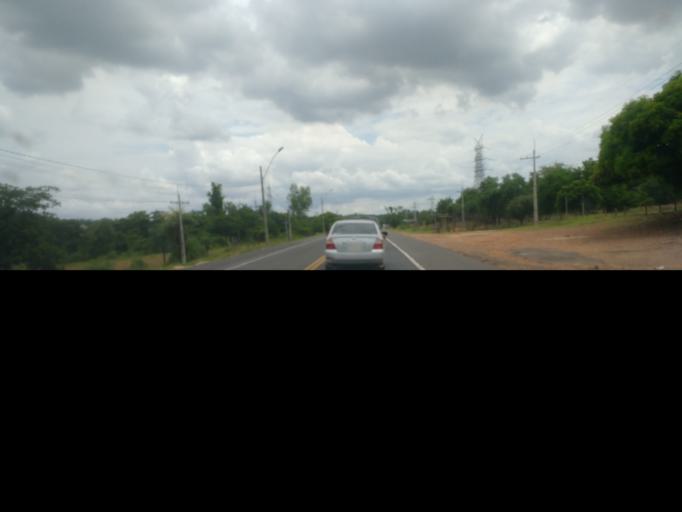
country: PY
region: Central
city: Limpio
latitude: -25.1357
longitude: -57.4499
